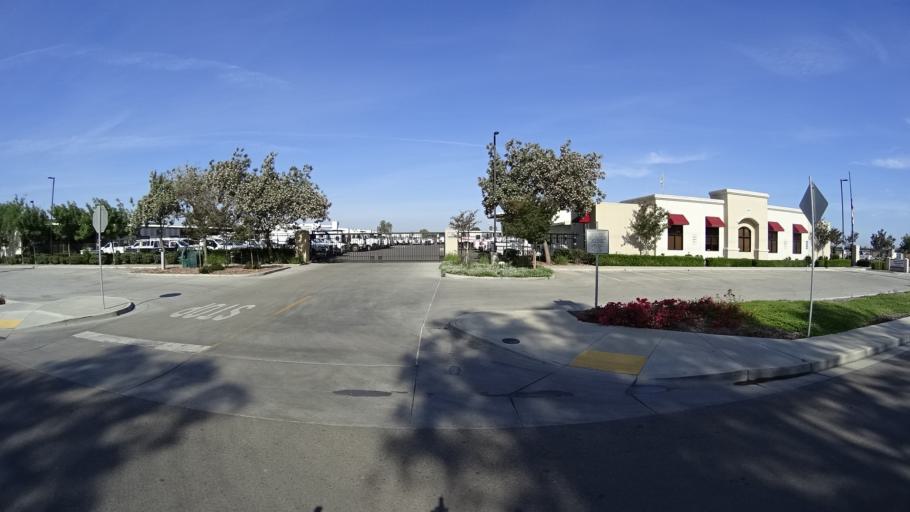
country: US
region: California
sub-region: Kings County
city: Home Garden
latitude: 36.3152
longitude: -119.6371
